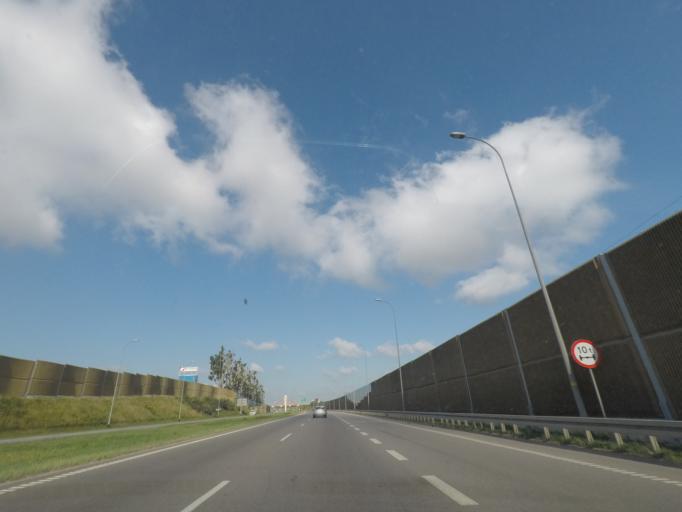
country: PL
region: Pomeranian Voivodeship
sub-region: Powiat gdanski
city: Kowale
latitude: 54.3474
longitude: 18.5331
